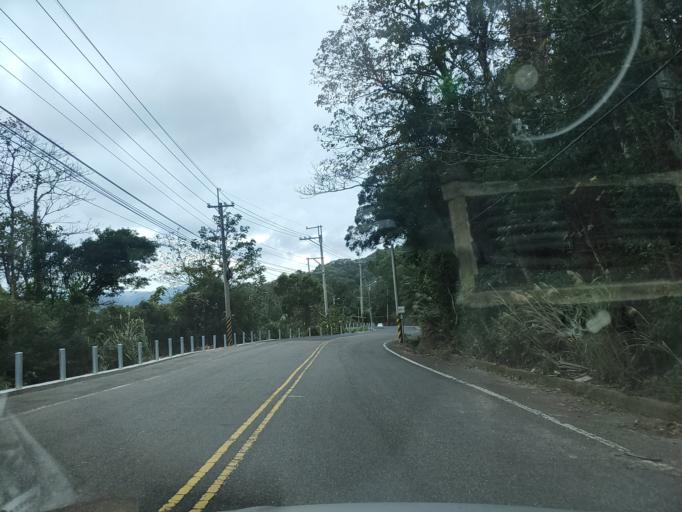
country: TW
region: Taiwan
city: Fengyuan
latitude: 24.3721
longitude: 120.7747
